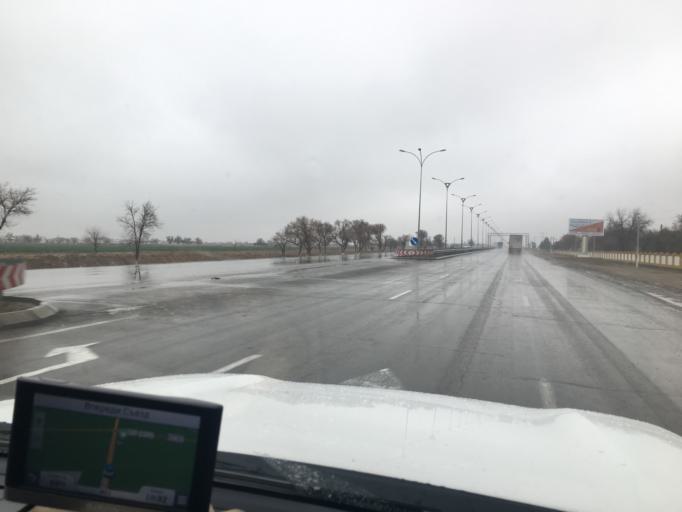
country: TM
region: Mary
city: Mary
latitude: 37.5796
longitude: 61.7840
